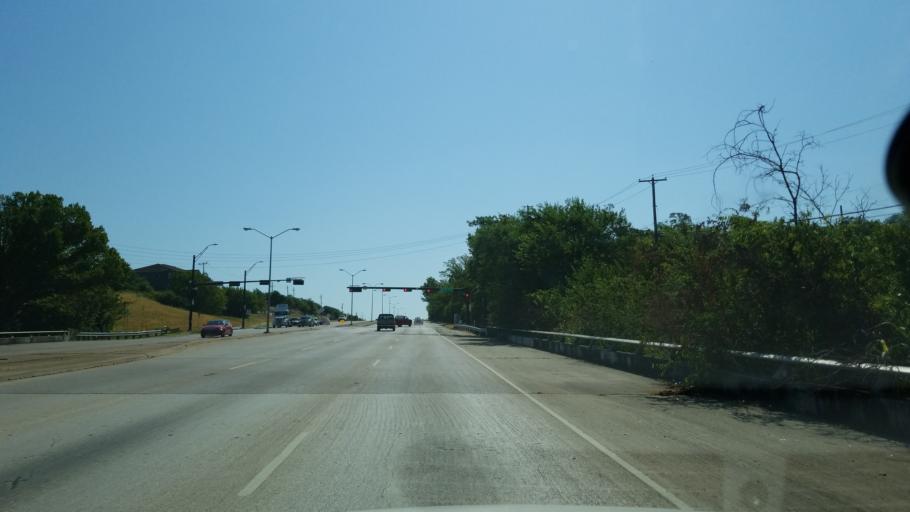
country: US
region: Texas
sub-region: Dallas County
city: Cockrell Hill
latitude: 32.7496
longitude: -96.9037
